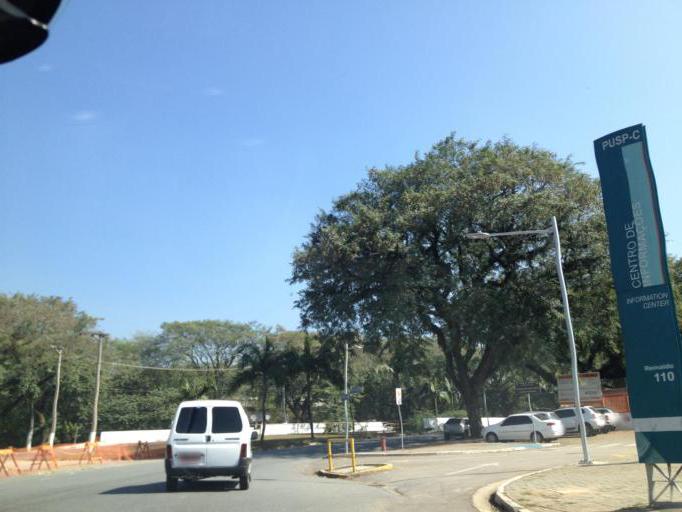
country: BR
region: Sao Paulo
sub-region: Sao Paulo
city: Sao Paulo
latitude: -23.5645
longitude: -46.7131
